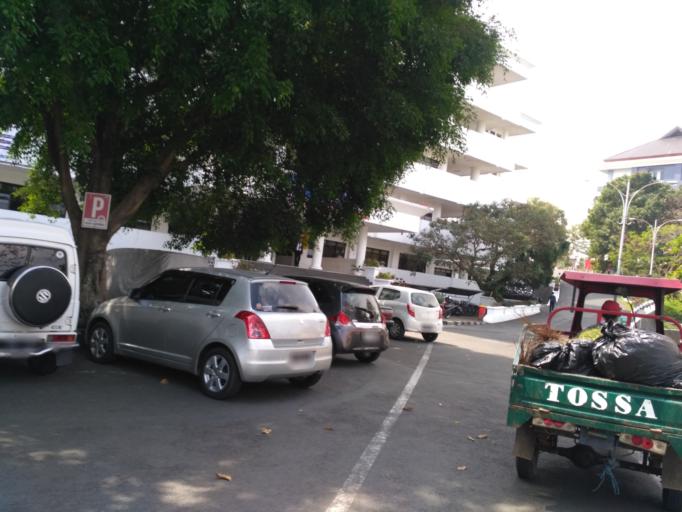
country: ID
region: East Java
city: Malang
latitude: -7.9216
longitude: 112.5987
